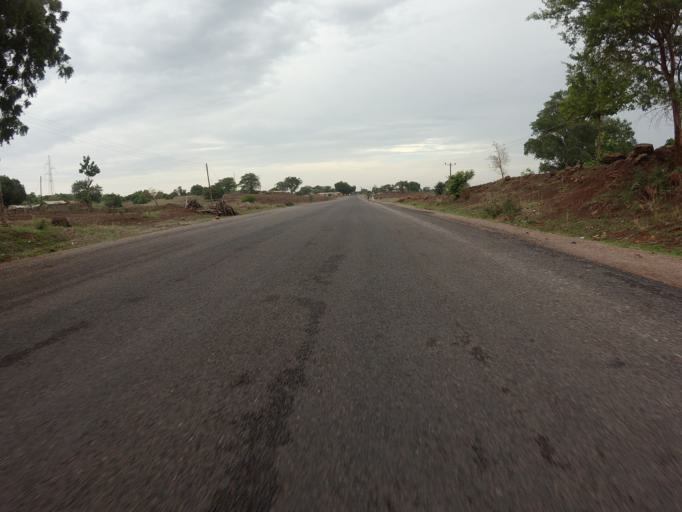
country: GH
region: Upper East
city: Bolgatanga
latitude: 10.8493
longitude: -0.6789
